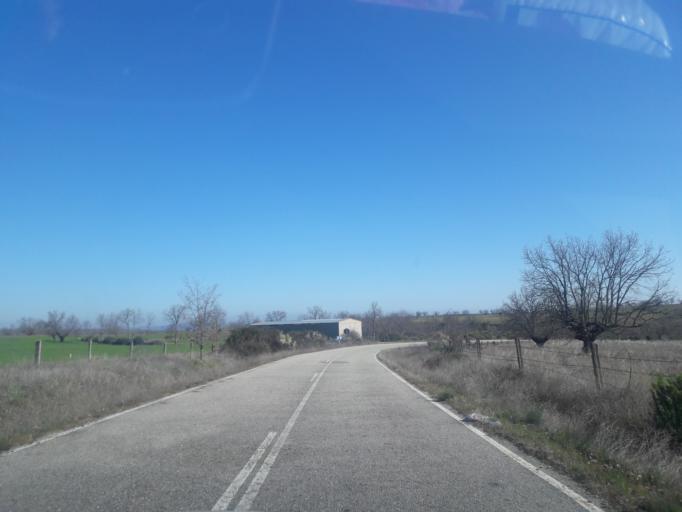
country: ES
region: Castille and Leon
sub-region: Provincia de Salamanca
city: Cabeza del Caballo
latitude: 41.1483
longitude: -6.5568
